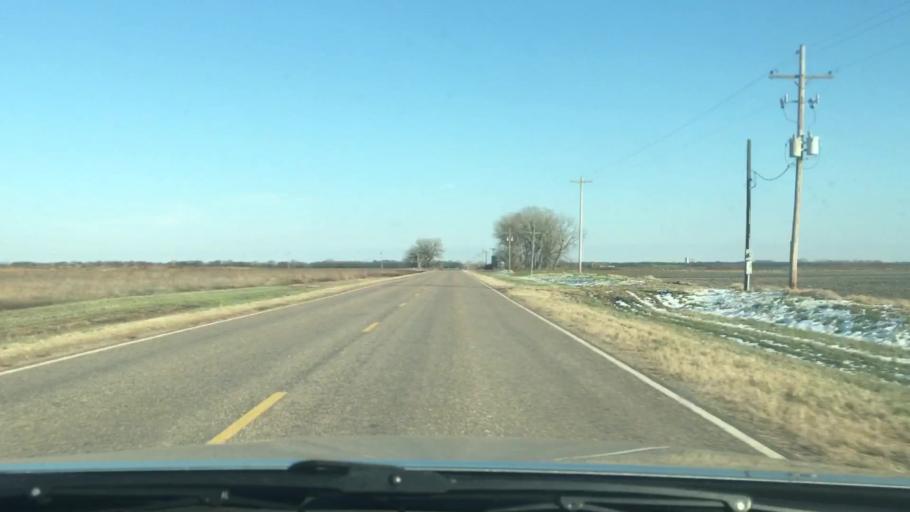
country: US
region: Kansas
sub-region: Rice County
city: Lyons
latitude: 38.2895
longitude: -98.1700
